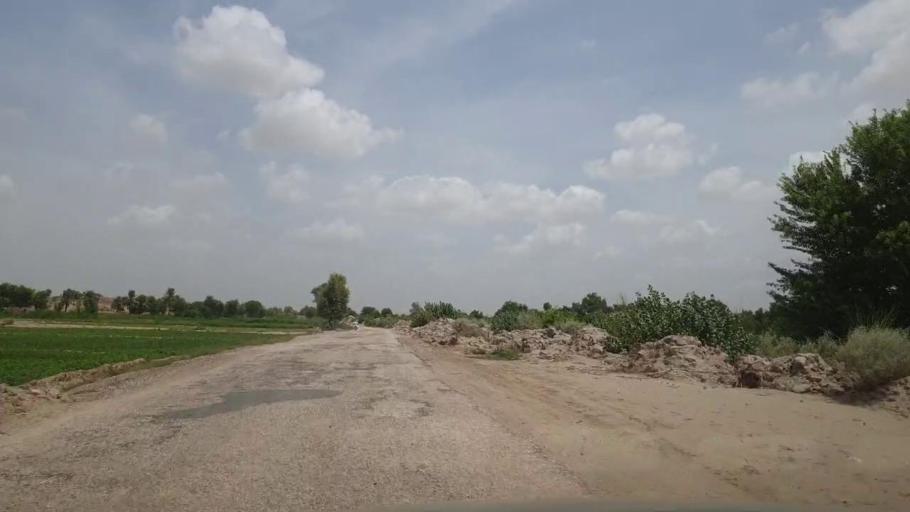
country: PK
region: Sindh
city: Kot Diji
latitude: 27.2166
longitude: 69.1057
